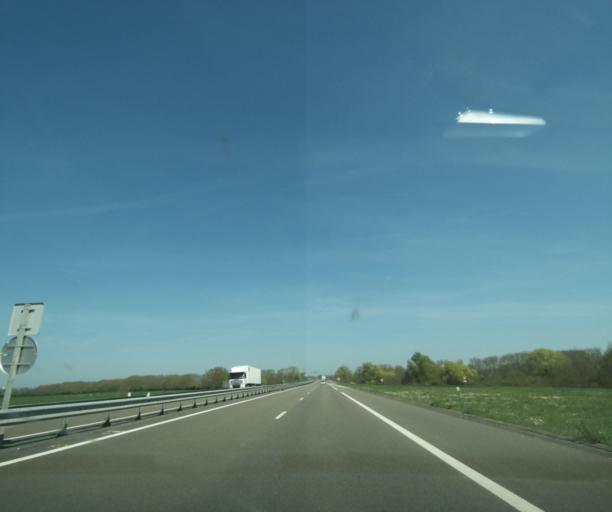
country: FR
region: Bourgogne
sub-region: Departement de la Nievre
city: Sermoise-sur-Loire
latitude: 46.9575
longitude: 3.1733
